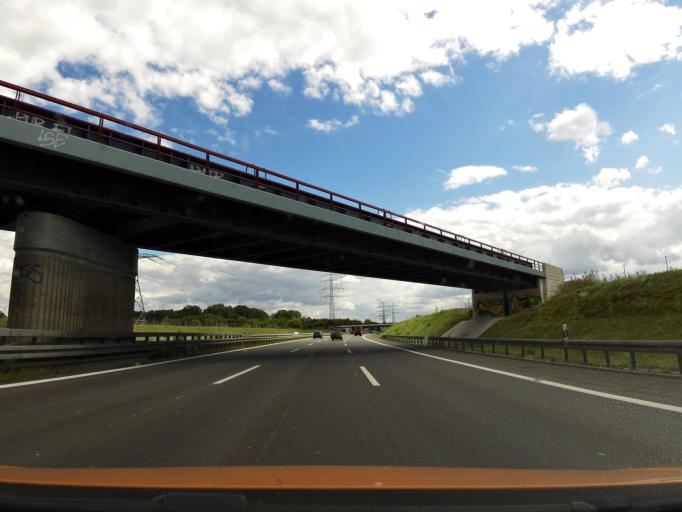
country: DE
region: Berlin
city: Karow
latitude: 52.6281
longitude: 13.4755
